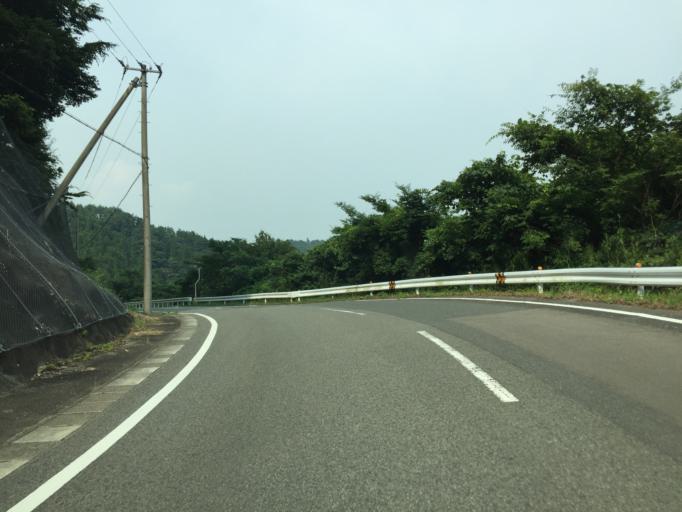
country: JP
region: Fukushima
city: Namie
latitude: 37.5897
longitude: 140.8928
